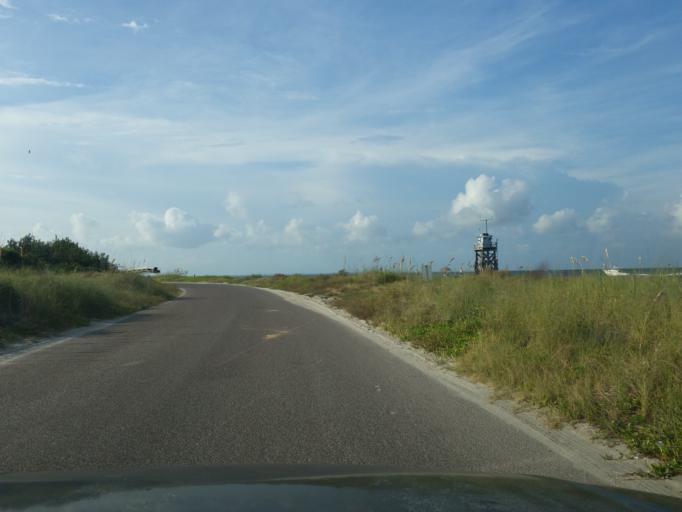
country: US
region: Alabama
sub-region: Mobile County
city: Dauphin Island
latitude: 30.2490
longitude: -88.0749
